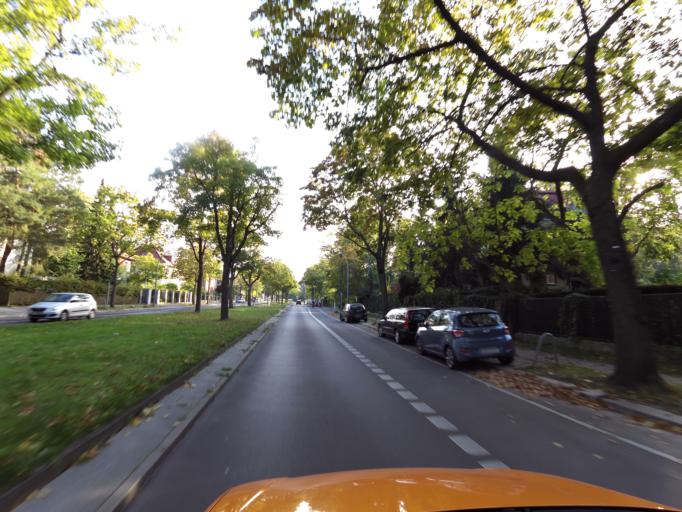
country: DE
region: Berlin
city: Dahlem
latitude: 52.4609
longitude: 13.3042
